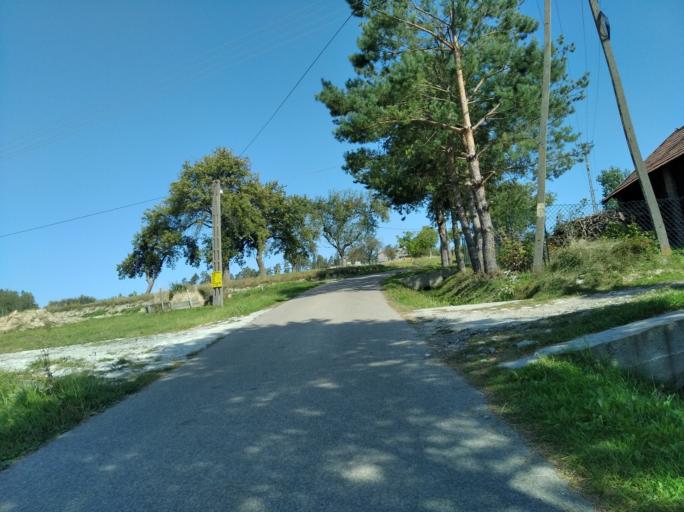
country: PL
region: Subcarpathian Voivodeship
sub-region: Powiat strzyzowski
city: Czudec
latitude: 49.9669
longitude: 21.8116
